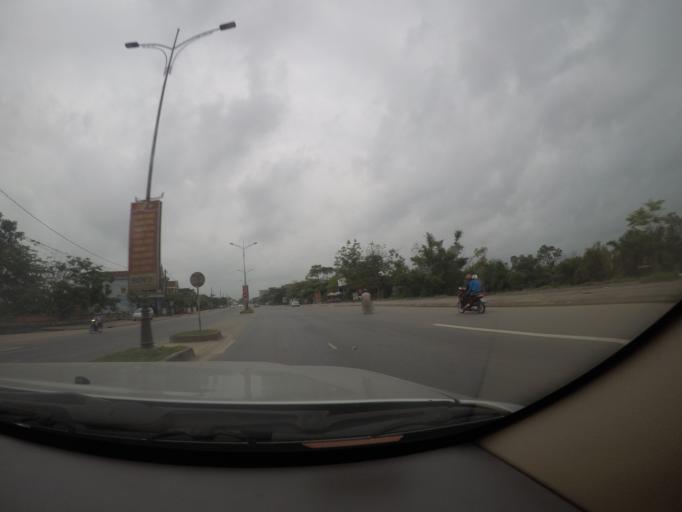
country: VN
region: Quang Tri
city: Ai Tu
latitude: 16.7466
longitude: 107.1779
